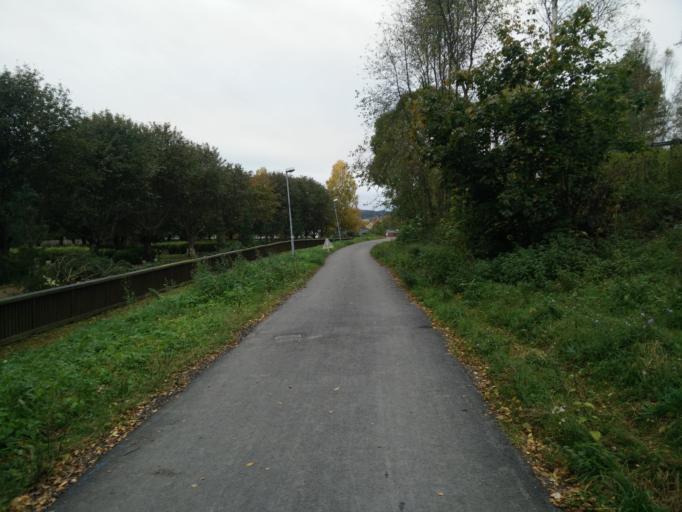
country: SE
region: Vaesternorrland
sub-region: Sundsvalls Kommun
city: Sundsvall
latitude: 62.3979
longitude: 17.2737
